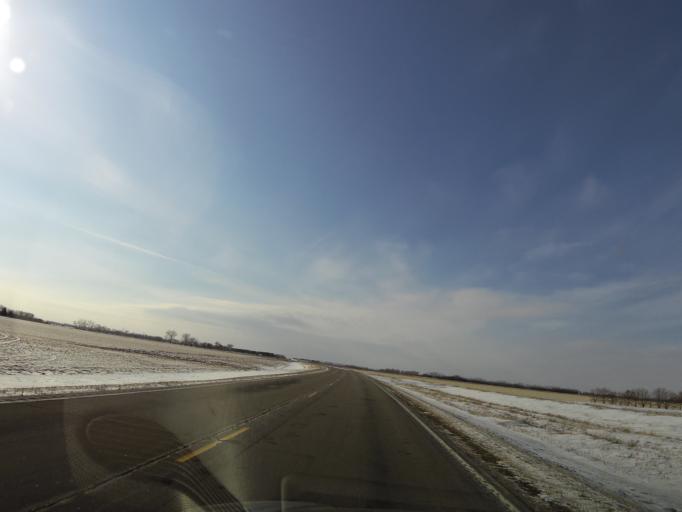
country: US
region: North Dakota
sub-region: Walsh County
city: Grafton
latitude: 48.4120
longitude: -97.1593
